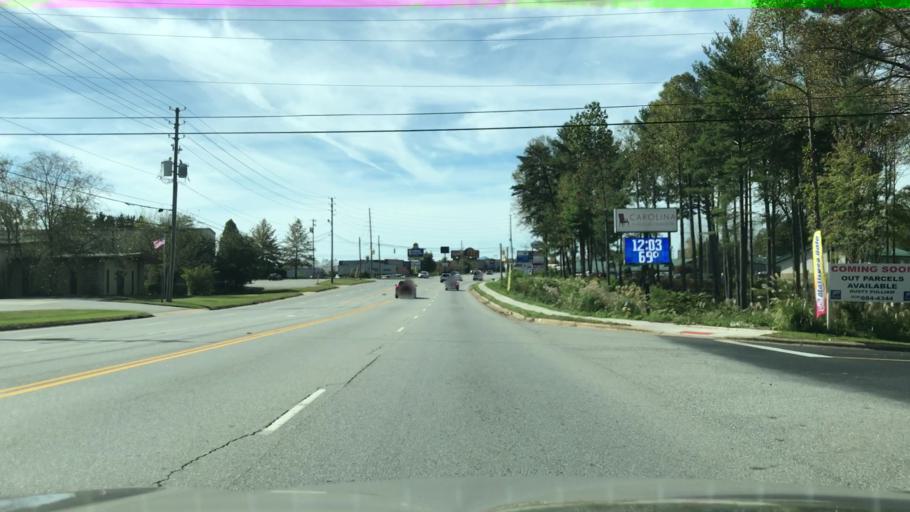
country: US
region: North Carolina
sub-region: Buncombe County
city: Royal Pines
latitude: 35.4539
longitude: -82.5226
